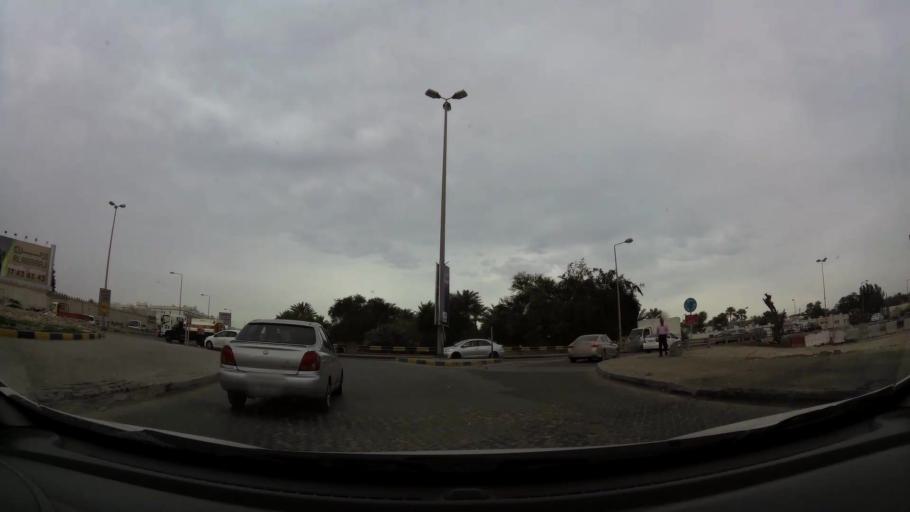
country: BH
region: Central Governorate
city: Madinat Hamad
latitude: 26.1442
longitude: 50.4931
